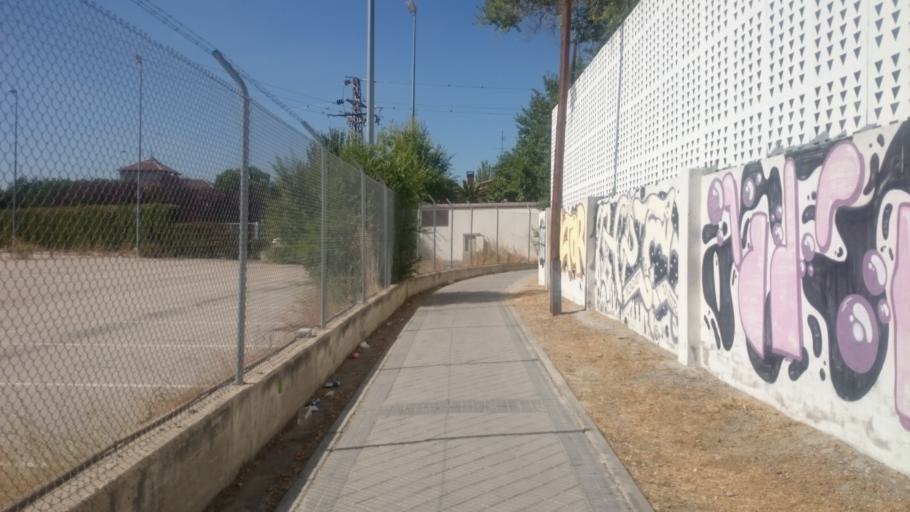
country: ES
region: Madrid
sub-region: Provincia de Madrid
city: Barajas de Madrid
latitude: 40.4676
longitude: -3.5801
